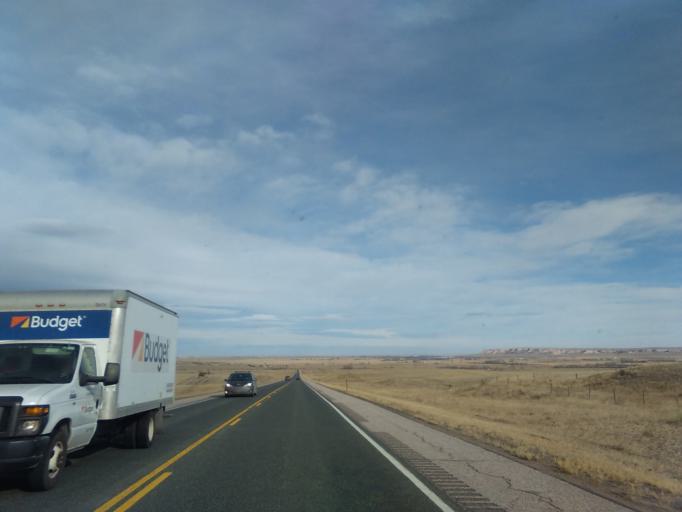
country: US
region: Wyoming
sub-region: Goshen County
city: Torrington
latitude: 41.6145
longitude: -104.2520
